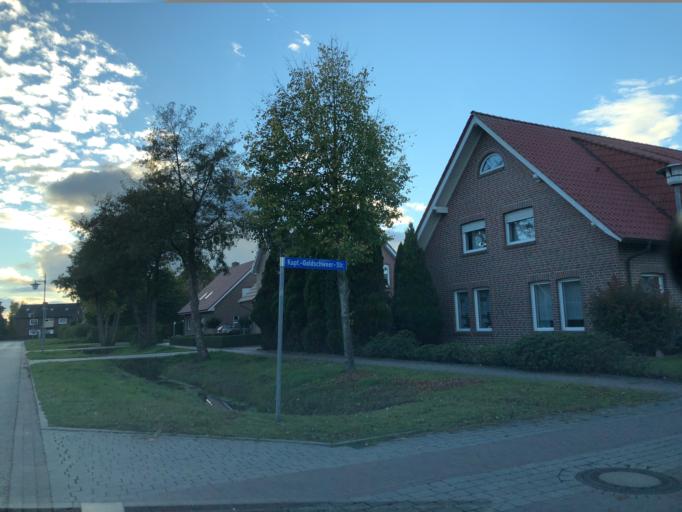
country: DE
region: Lower Saxony
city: Papenburg
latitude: 53.0843
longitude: 7.4131
